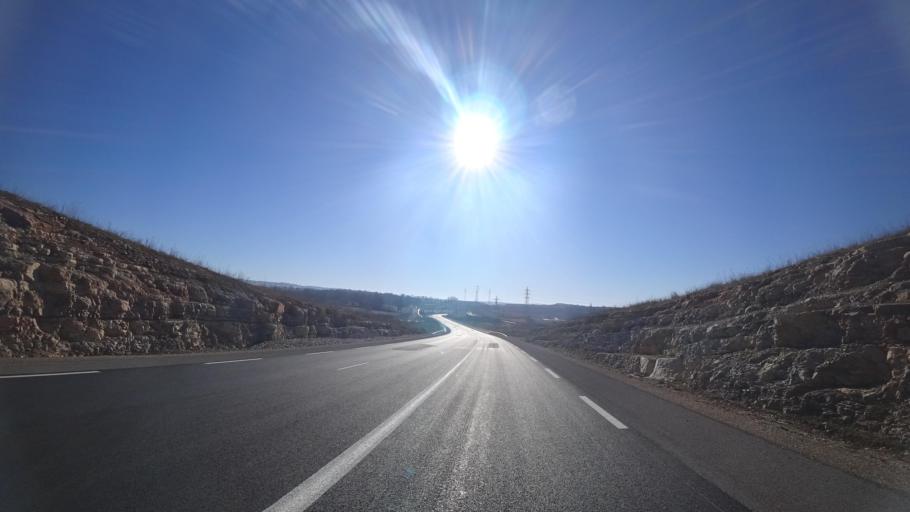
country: FR
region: Midi-Pyrenees
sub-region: Departement de l'Aveyron
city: Sebazac-Concoures
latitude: 44.3883
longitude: 2.6134
